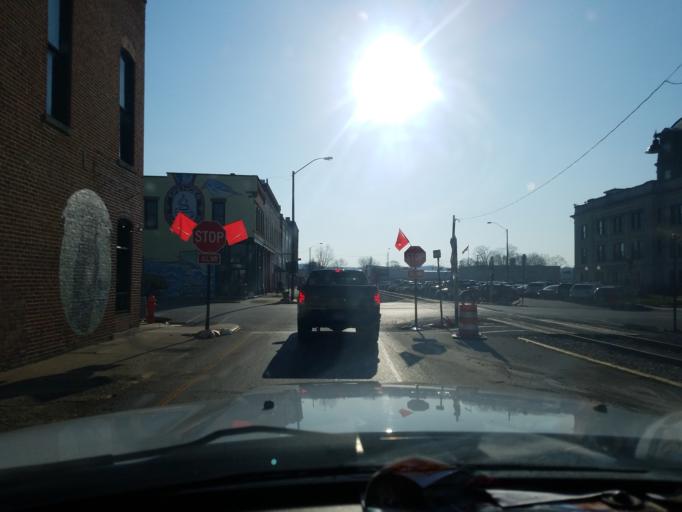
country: US
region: Indiana
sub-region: Owen County
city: Spencer
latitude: 39.2861
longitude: -86.7629
